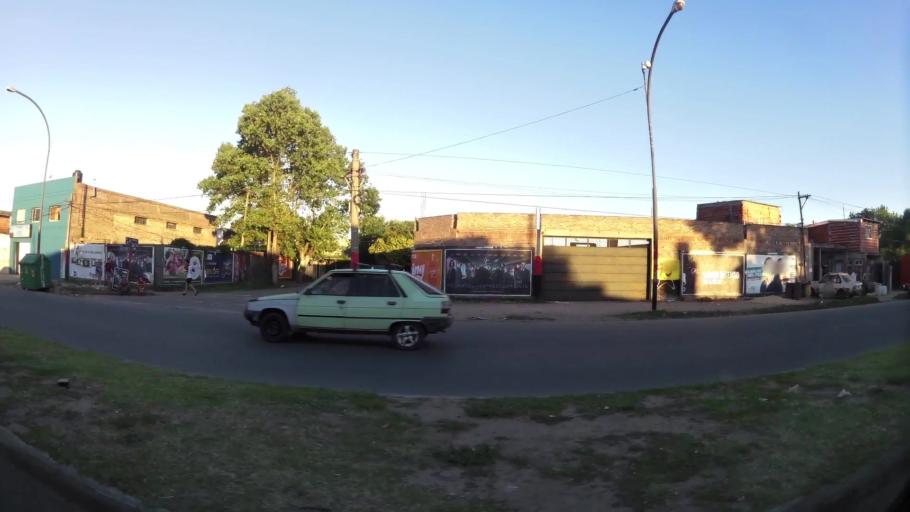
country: AR
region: Santa Fe
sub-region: Departamento de Rosario
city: Rosario
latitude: -32.9679
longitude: -60.6864
